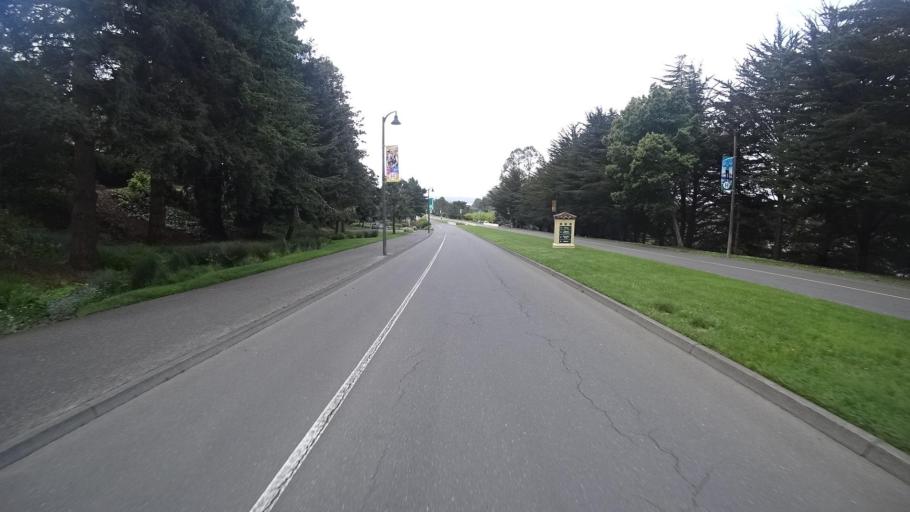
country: US
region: California
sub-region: Humboldt County
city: Arcata
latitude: 40.8765
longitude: -124.0813
